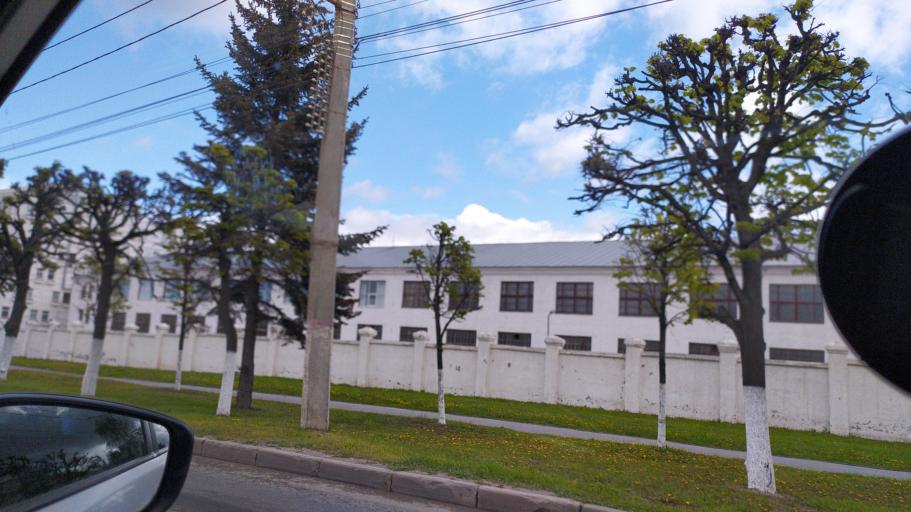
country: RU
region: Chuvashia
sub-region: Cheboksarskiy Rayon
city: Cheboksary
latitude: 56.1334
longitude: 47.2828
